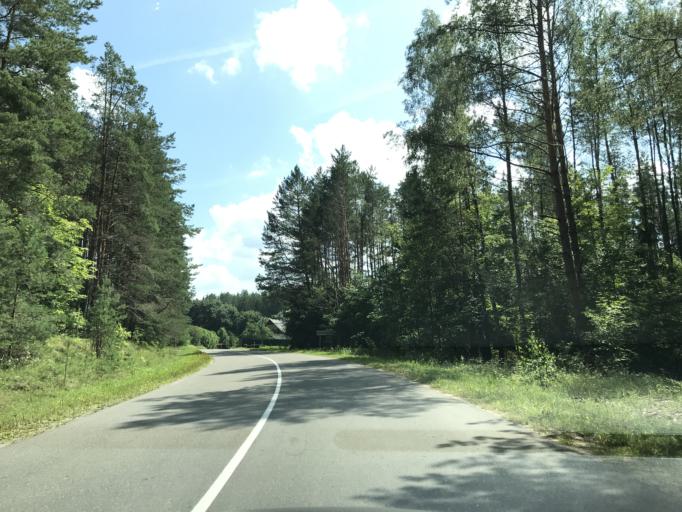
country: BY
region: Minsk
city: Rakaw
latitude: 53.9964
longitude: 26.9875
